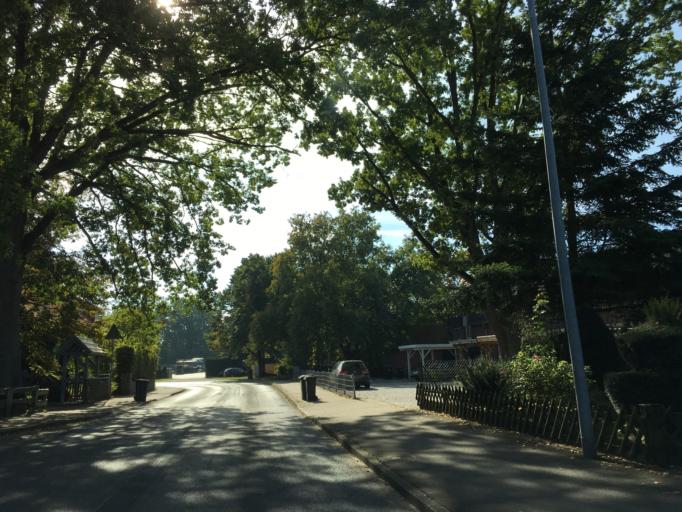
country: DE
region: Lower Saxony
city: Adendorf
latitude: 53.2754
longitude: 10.4742
